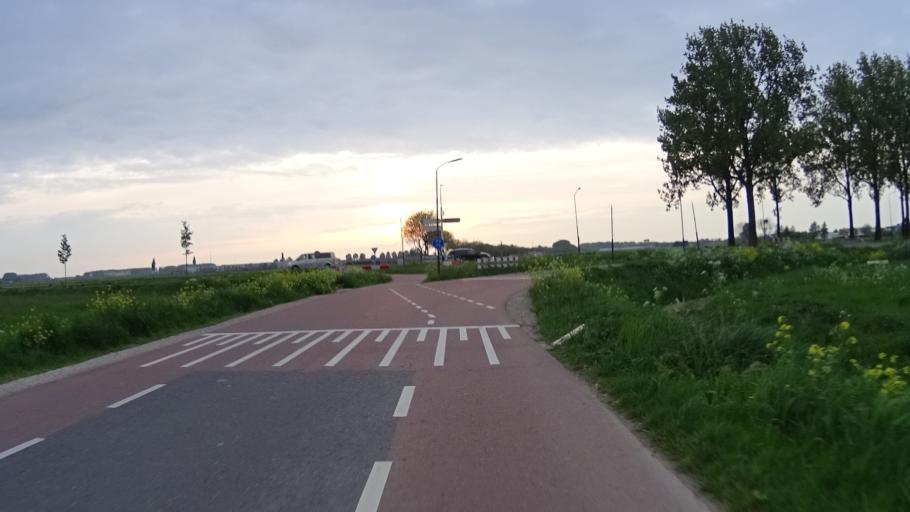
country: NL
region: North Brabant
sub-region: Gemeente Woudrichem
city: Woudrichem
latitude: 51.7774
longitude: 5.0523
